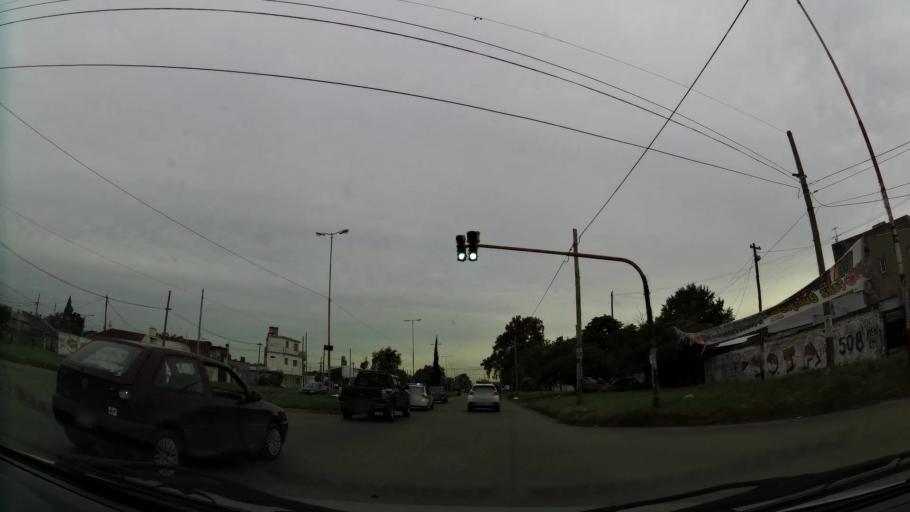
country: AR
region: Buenos Aires
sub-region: Partido de Lanus
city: Lanus
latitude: -34.7177
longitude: -58.3505
